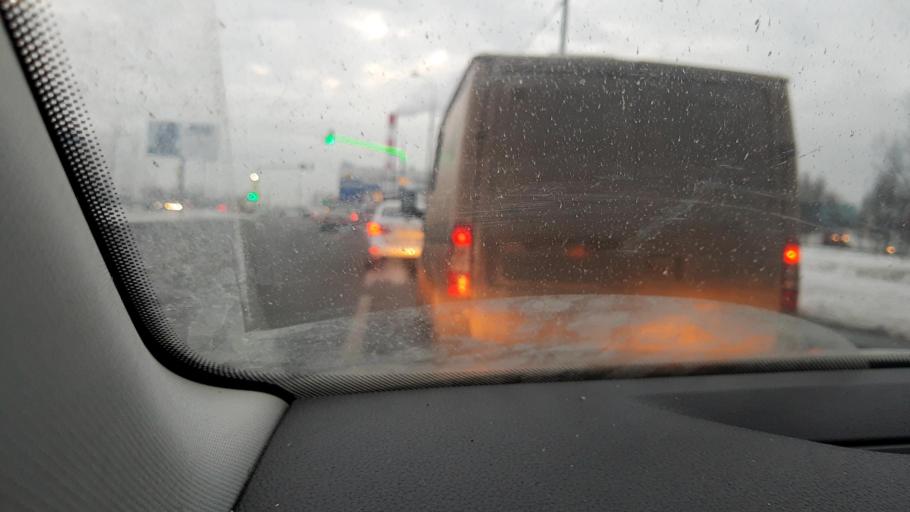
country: RU
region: Moskovskaya
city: Kommunarka
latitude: 55.5525
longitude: 37.5357
